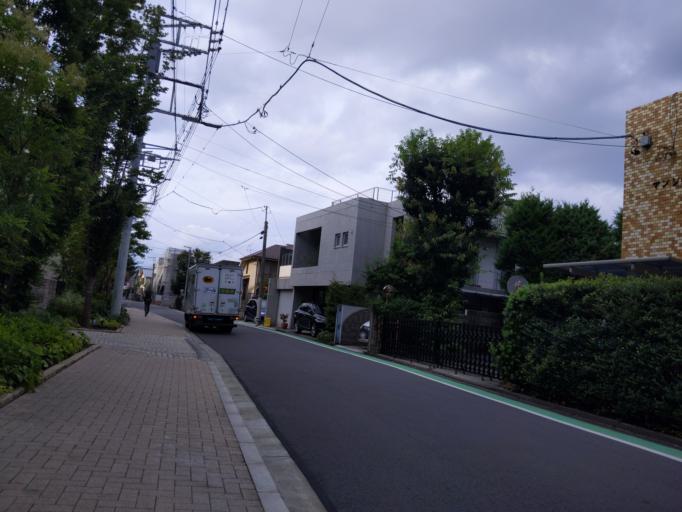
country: JP
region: Tokyo
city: Chofugaoka
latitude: 35.6384
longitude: 139.5847
